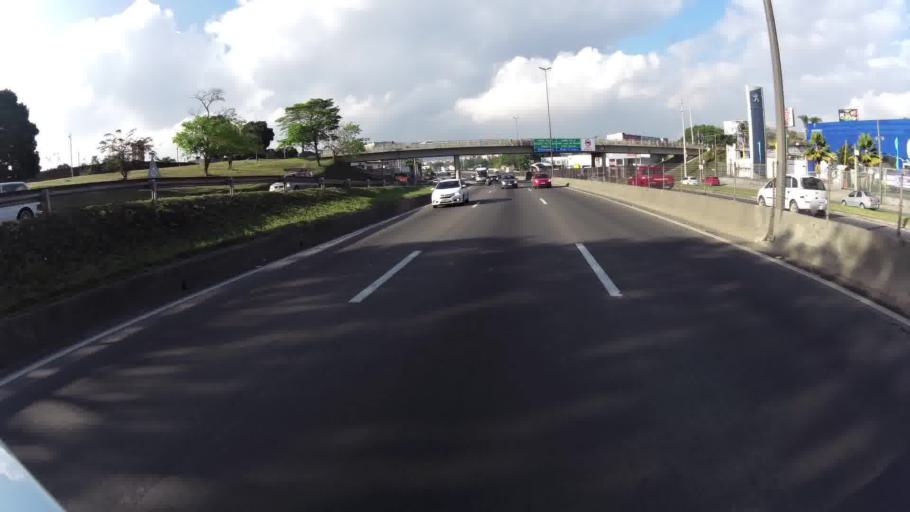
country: BR
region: Rio de Janeiro
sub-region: Duque De Caxias
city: Duque de Caxias
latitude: -22.7994
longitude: -43.2901
